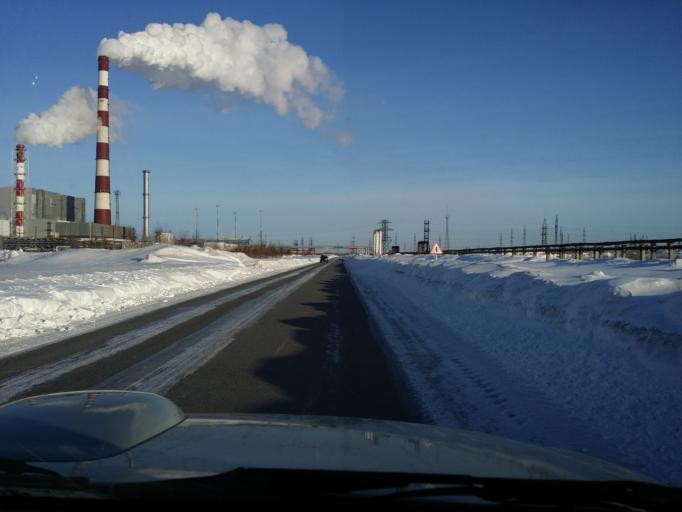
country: RU
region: Khanty-Mansiyskiy Avtonomnyy Okrug
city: Izluchinsk
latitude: 60.9773
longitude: 76.9263
